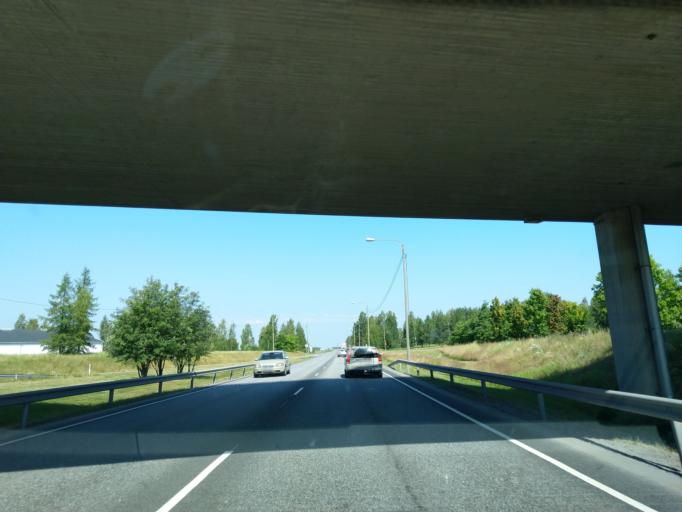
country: FI
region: Satakunta
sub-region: Pori
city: Nakkila
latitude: 61.3619
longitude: 21.9947
